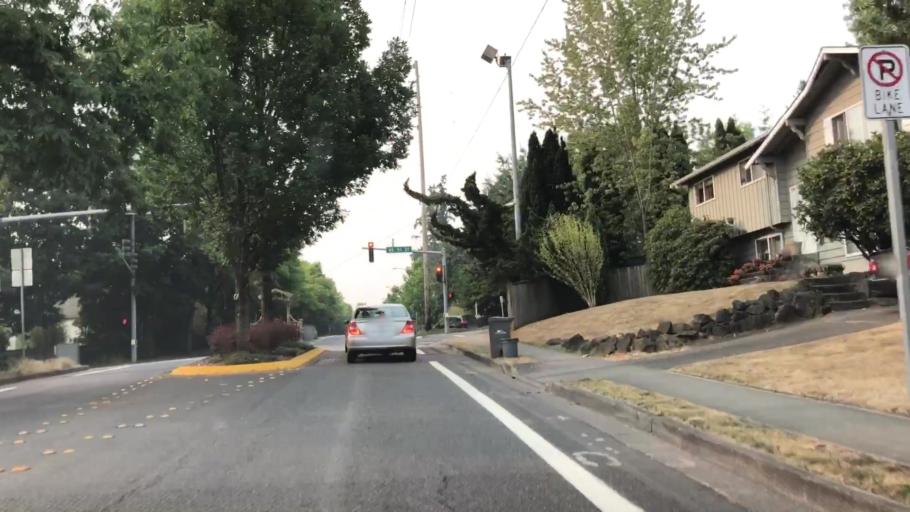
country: US
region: Washington
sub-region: King County
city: Redmond
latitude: 47.6546
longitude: -122.1325
